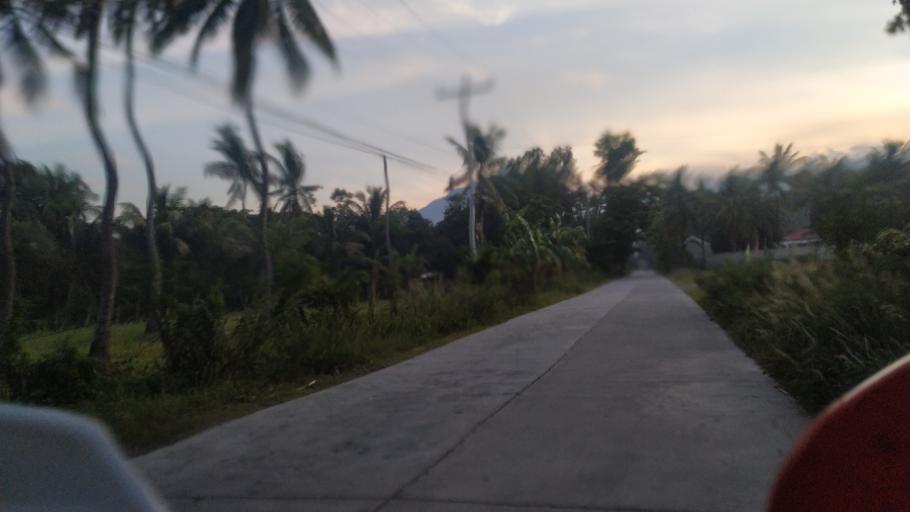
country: PH
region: Central Visayas
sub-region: Province of Negros Oriental
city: Valencia
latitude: 9.3193
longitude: 123.2625
